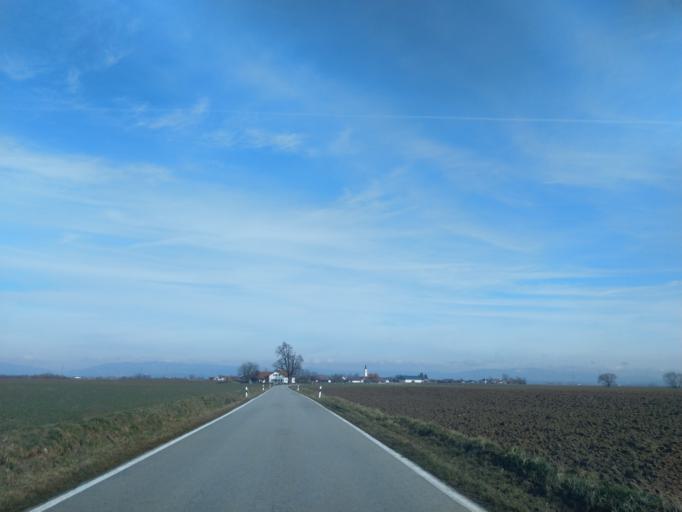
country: DE
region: Bavaria
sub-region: Lower Bavaria
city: Buchhofen
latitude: 48.6788
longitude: 12.9382
